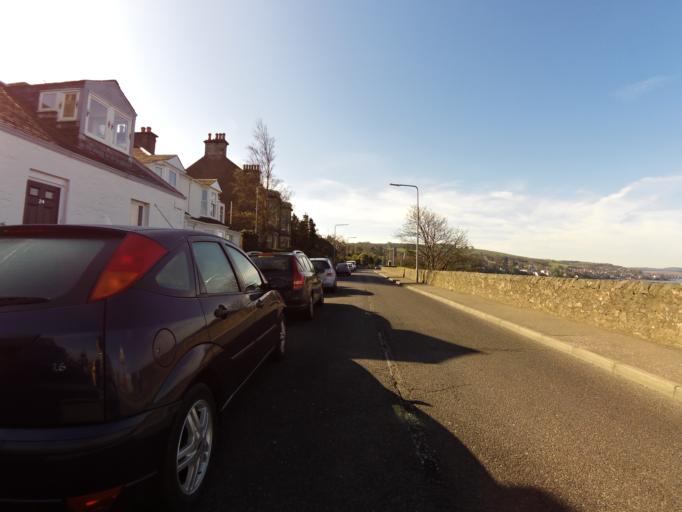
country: GB
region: Scotland
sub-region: Fife
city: Newport-On-Tay
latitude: 56.4417
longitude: -2.9407
